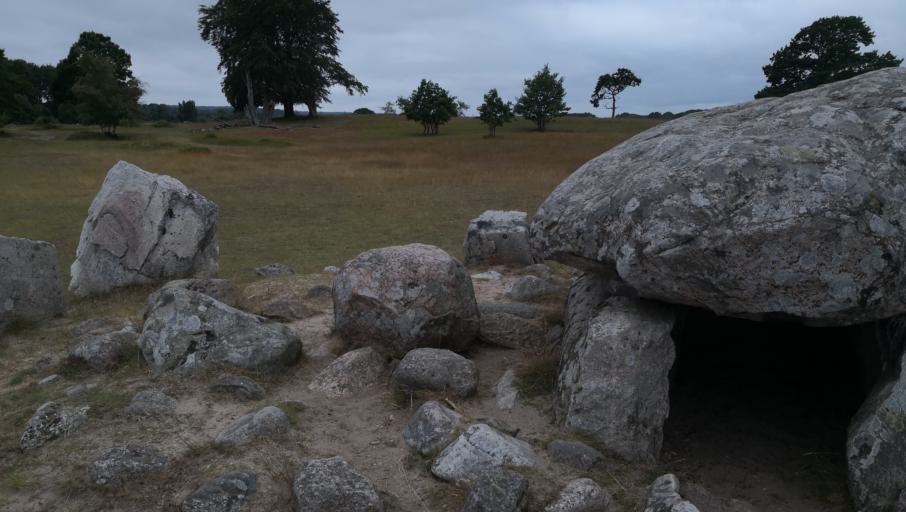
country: SE
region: Skane
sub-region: Simrishamns Kommun
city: Kivik
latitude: 55.7261
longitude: 14.1946
